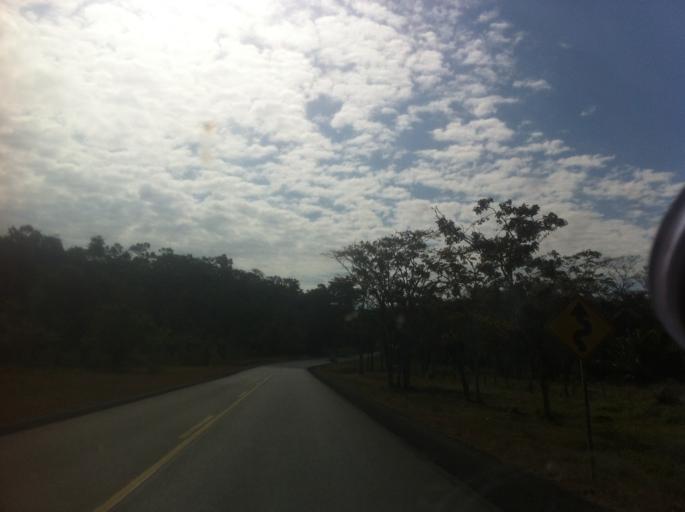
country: NI
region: Rio San Juan
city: San Miguelito
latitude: 11.3859
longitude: -84.7933
